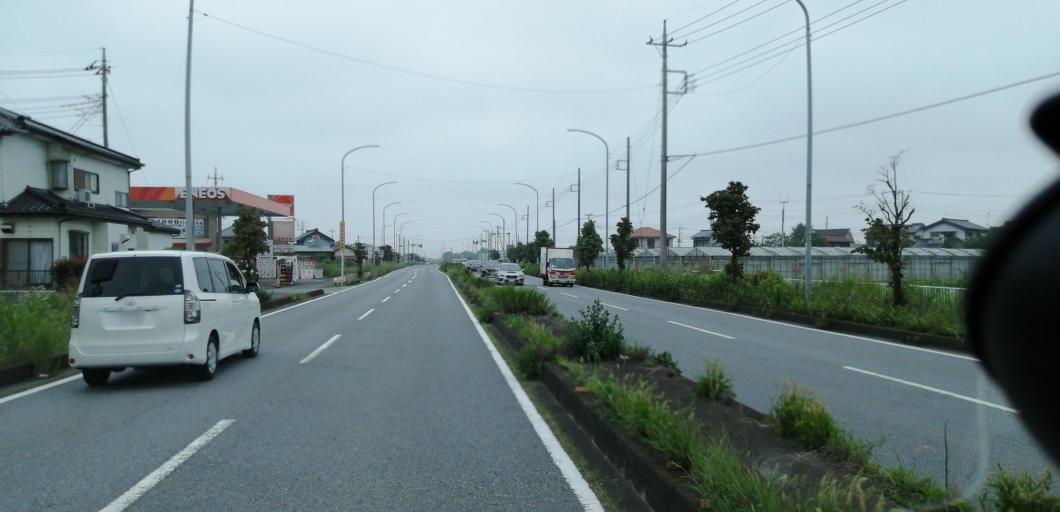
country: JP
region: Saitama
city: Kazo
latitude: 36.1358
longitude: 139.5985
